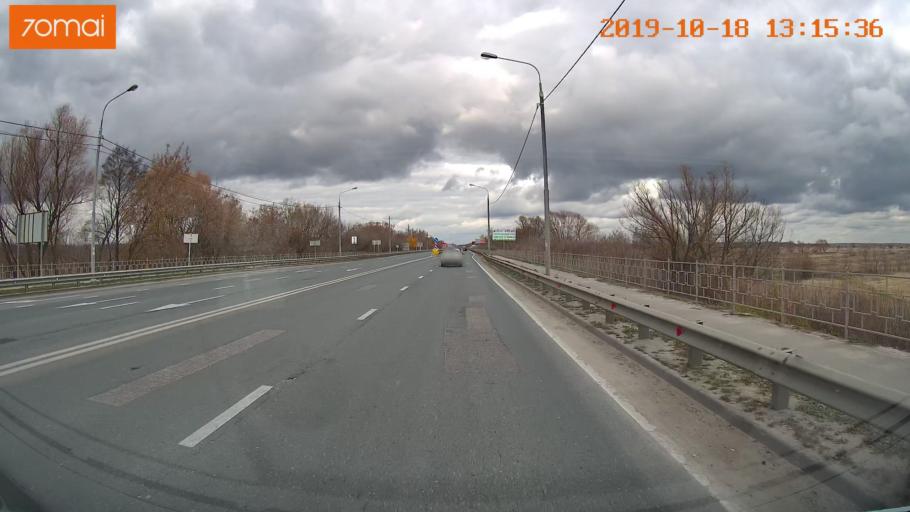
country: RU
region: Rjazan
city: Polyany
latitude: 54.6390
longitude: 39.7831
